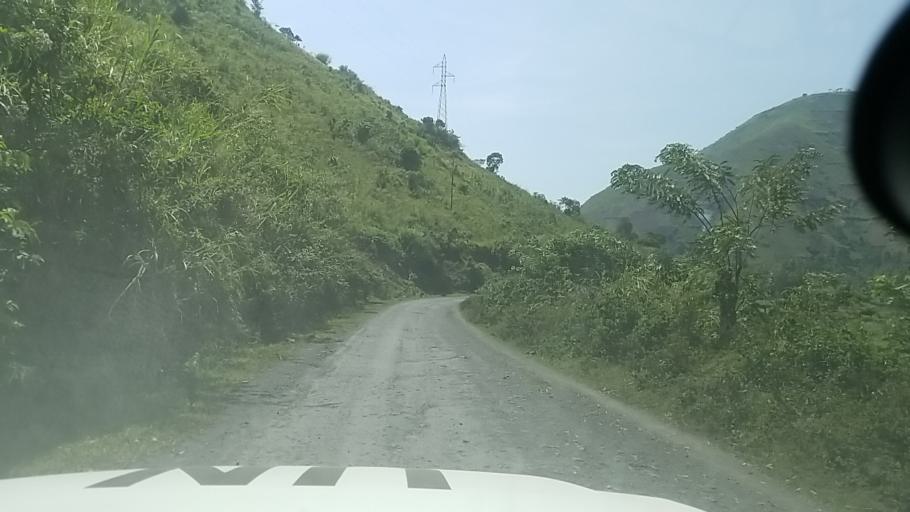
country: CD
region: Nord Kivu
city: Sake
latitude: -1.7640
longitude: 28.9945
